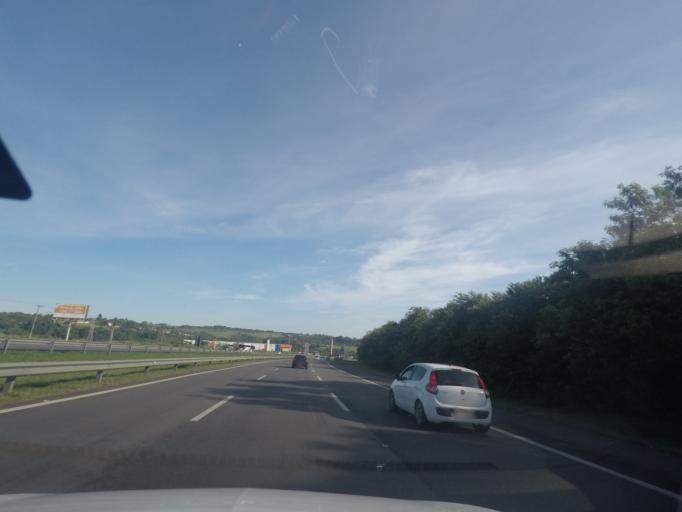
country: BR
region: Sao Paulo
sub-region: Americana
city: Americana
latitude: -22.6951
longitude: -47.3103
